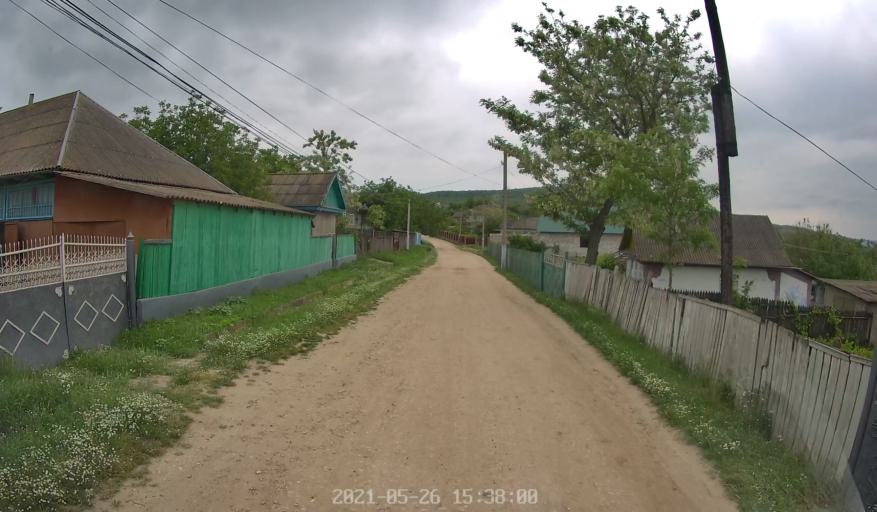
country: MD
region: Hincesti
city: Dancu
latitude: 46.6691
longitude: 28.3189
